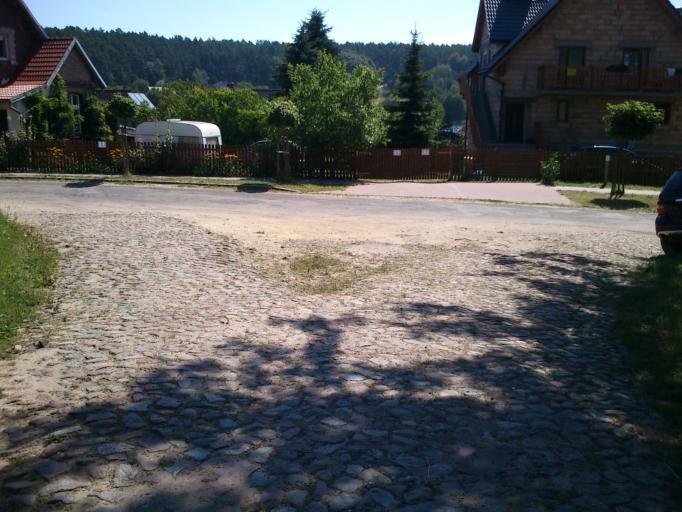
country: PL
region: West Pomeranian Voivodeship
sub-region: Powiat kamienski
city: Miedzyzdroje
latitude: 53.9627
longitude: 14.5714
